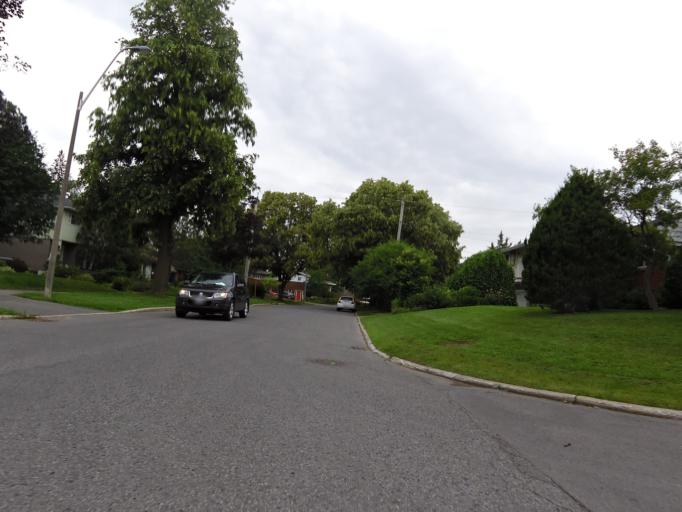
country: CA
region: Ontario
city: Bells Corners
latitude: 45.3562
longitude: -75.7842
